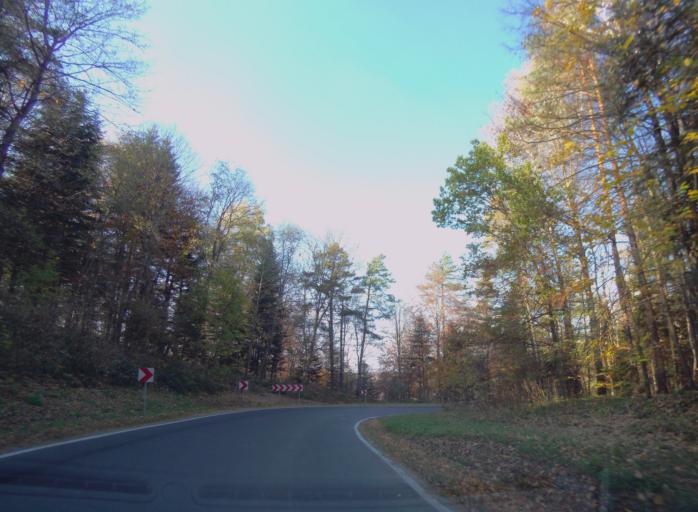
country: PL
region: Subcarpathian Voivodeship
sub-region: Powiat leski
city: Polanczyk
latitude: 49.3954
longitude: 22.4343
